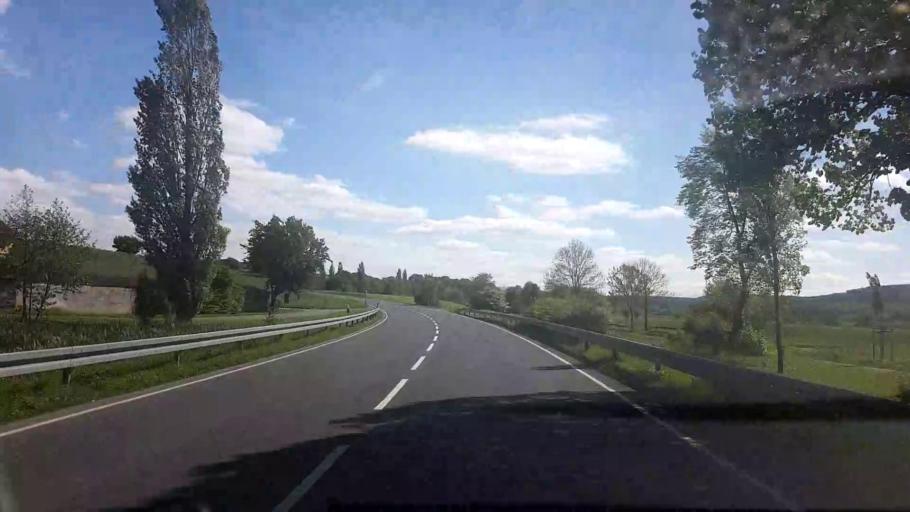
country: DE
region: Bavaria
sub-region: Regierungsbezirk Unterfranken
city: Untermerzbach
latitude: 50.1011
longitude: 10.8654
